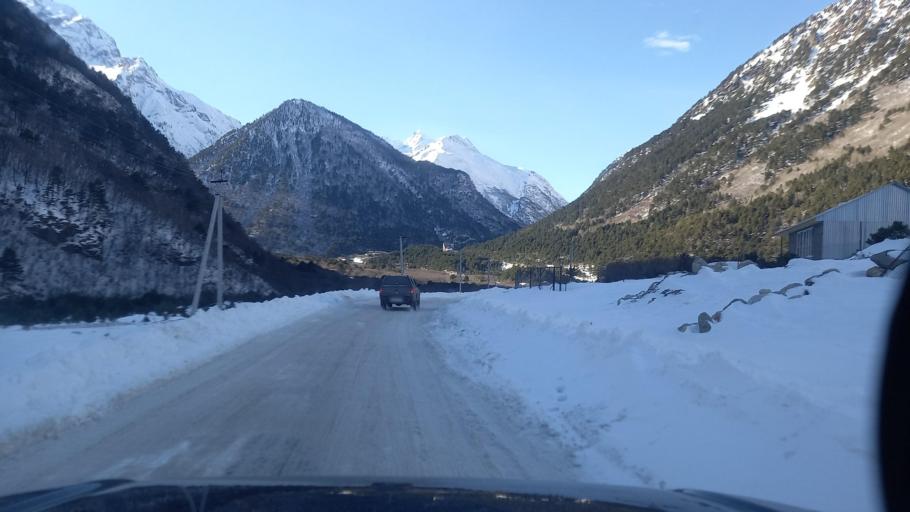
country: RU
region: Kabardino-Balkariya
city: Verkhnyaya Balkariya
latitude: 42.8997
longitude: 43.6237
